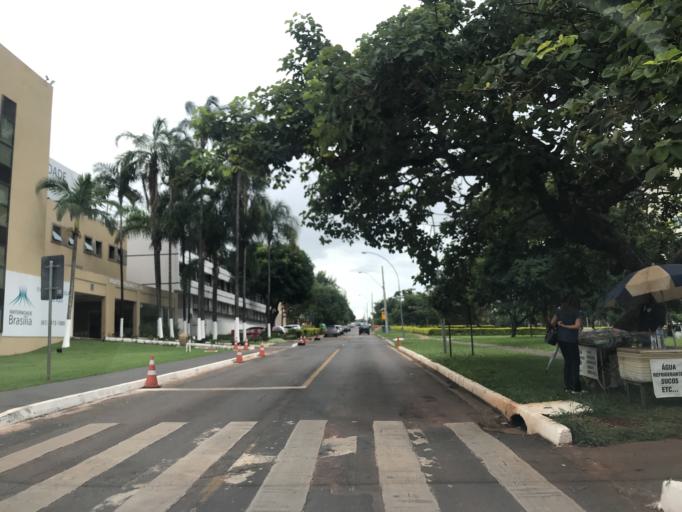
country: BR
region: Federal District
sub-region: Brasilia
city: Brasilia
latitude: -15.7931
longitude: -47.9197
